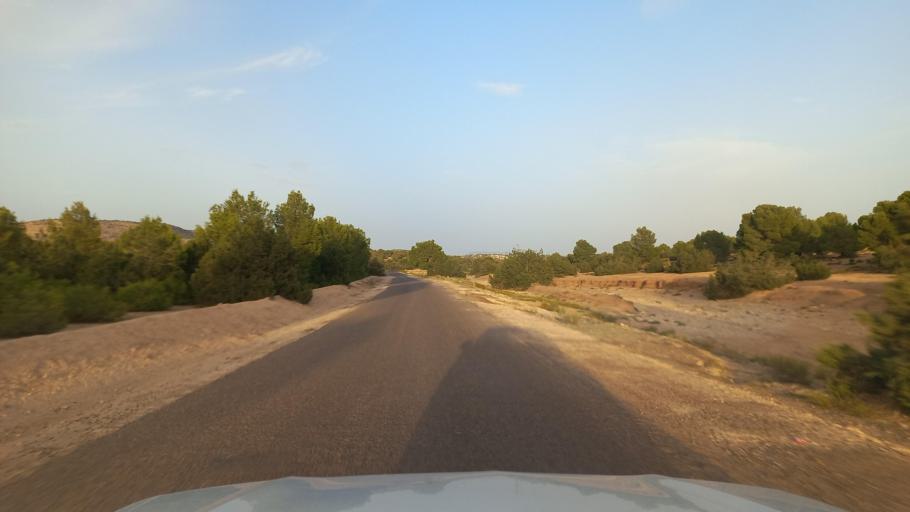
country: TN
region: Al Qasrayn
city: Sbiba
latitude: 35.4104
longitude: 8.9224
